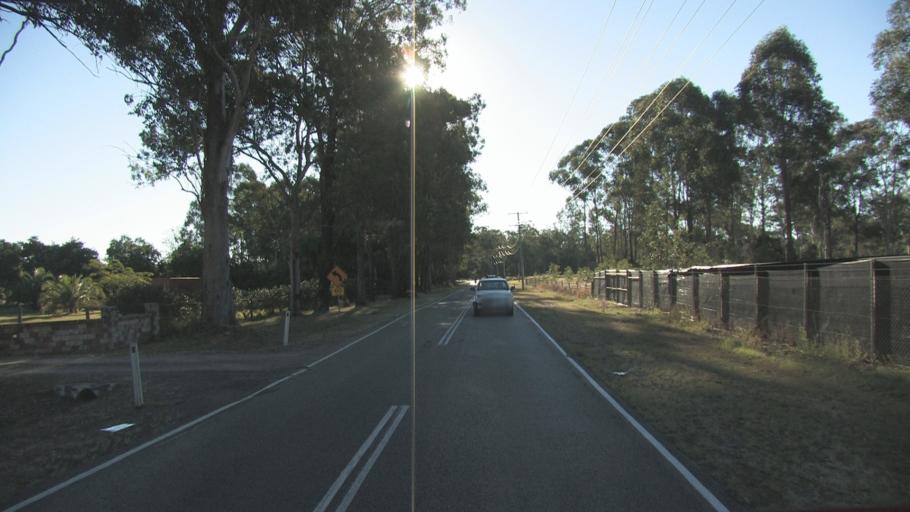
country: AU
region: Queensland
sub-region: Logan
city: Chambers Flat
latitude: -27.7484
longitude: 153.0756
